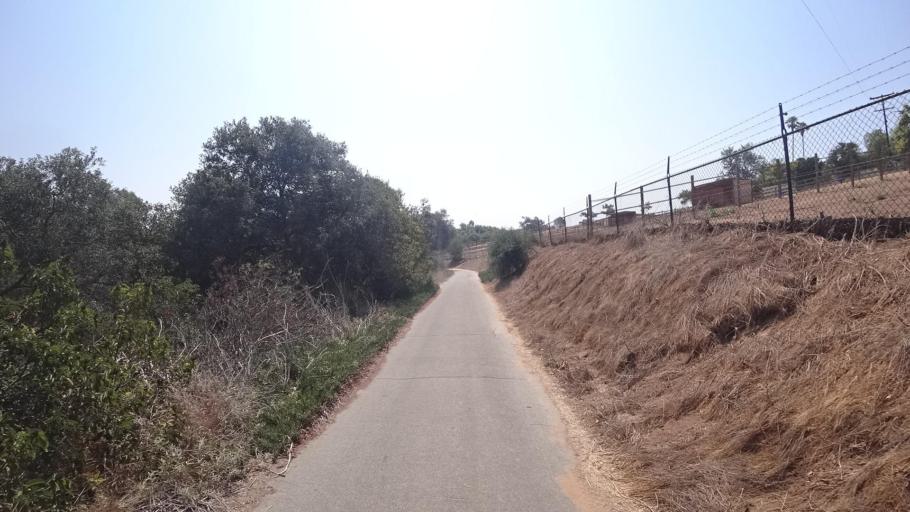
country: US
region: California
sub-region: San Diego County
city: Bonsall
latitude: 33.2887
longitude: -117.2580
